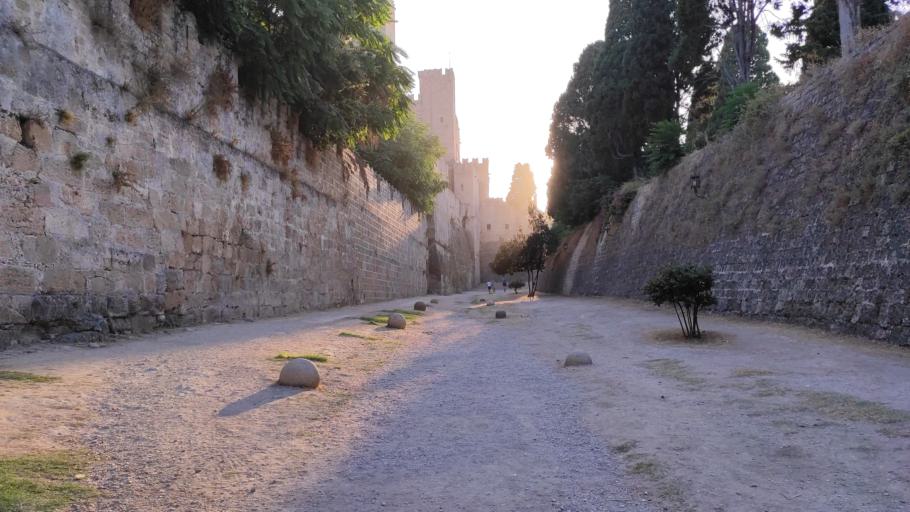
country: GR
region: South Aegean
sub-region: Nomos Dodekanisou
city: Rodos
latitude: 36.4461
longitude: 28.2255
